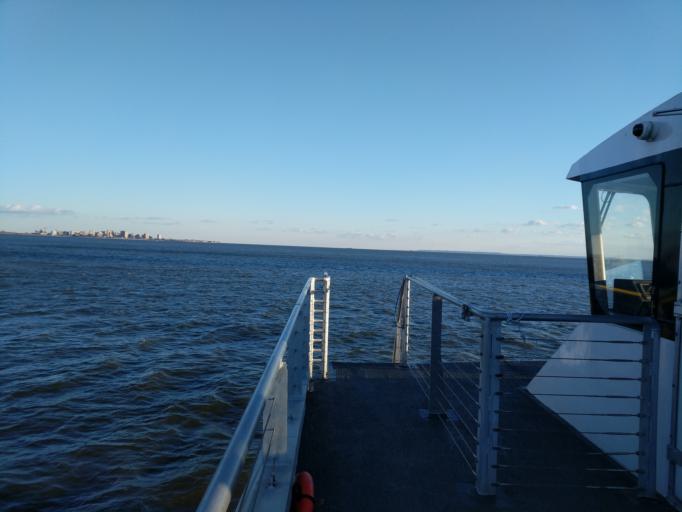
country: US
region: New York
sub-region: Kings County
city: Bensonhurst
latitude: 40.6086
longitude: -74.0403
